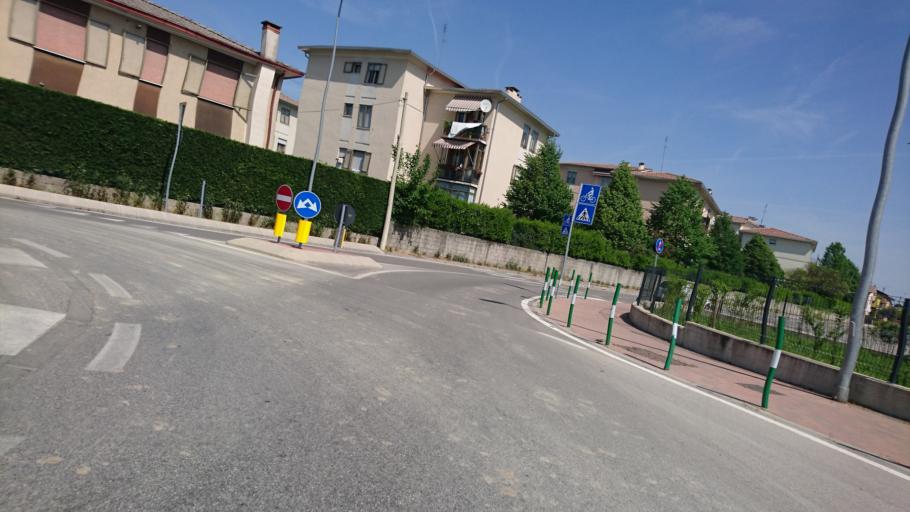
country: IT
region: Veneto
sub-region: Provincia di Padova
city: Vigodarzere
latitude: 45.4475
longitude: 11.8767
